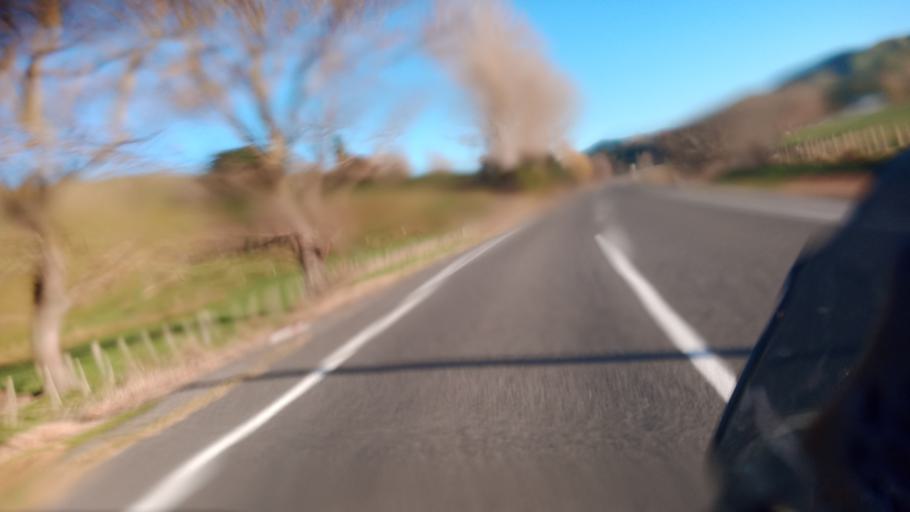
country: NZ
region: Hawke's Bay
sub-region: Wairoa District
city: Wairoa
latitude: -39.0169
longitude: 177.3605
